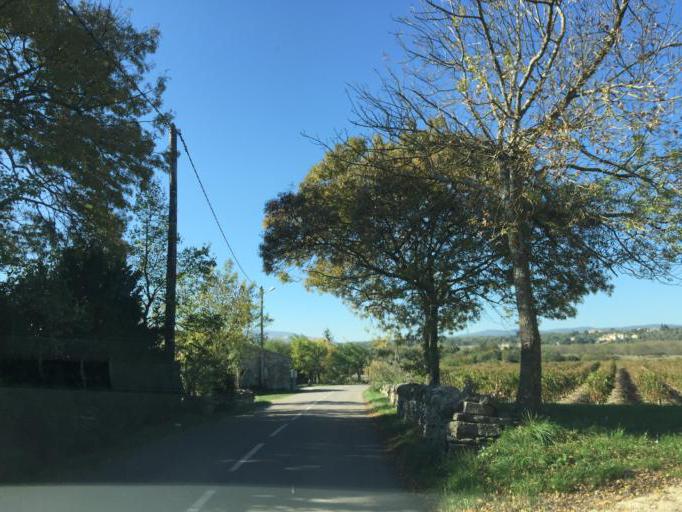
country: FR
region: Rhone-Alpes
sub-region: Departement de l'Ardeche
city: Bourg-Saint-Andeol
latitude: 44.4486
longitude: 4.5974
